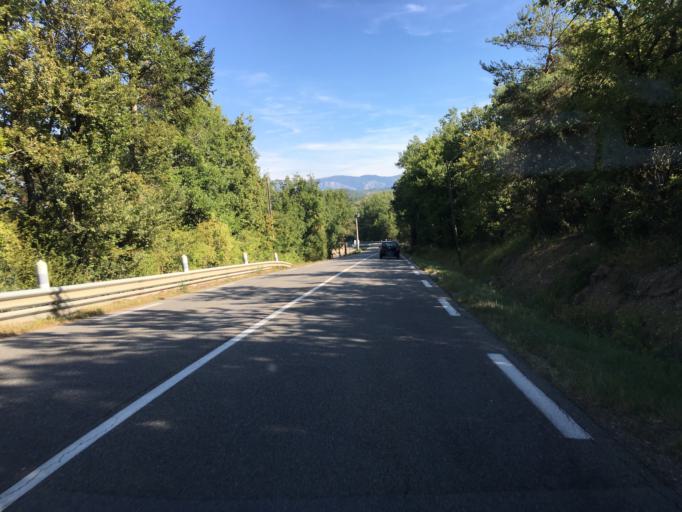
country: FR
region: Provence-Alpes-Cote d'Azur
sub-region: Departement des Hautes-Alpes
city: Laragne-Monteglin
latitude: 44.2899
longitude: 5.8425
